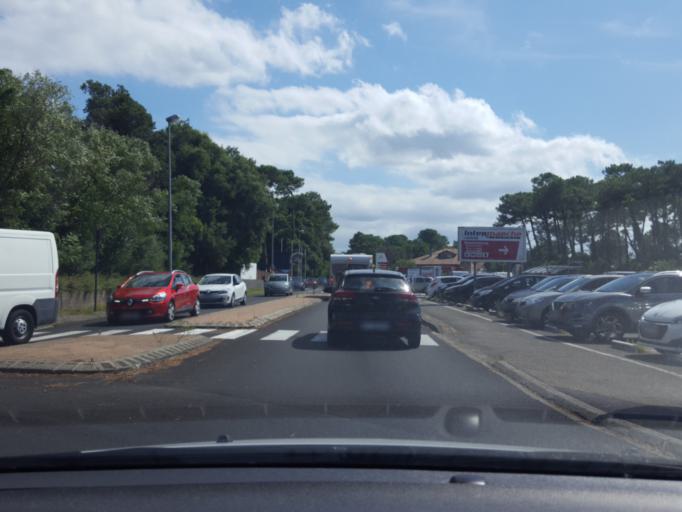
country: FR
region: Aquitaine
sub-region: Departement des Landes
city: Capbreton
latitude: 43.6390
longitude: -1.4259
